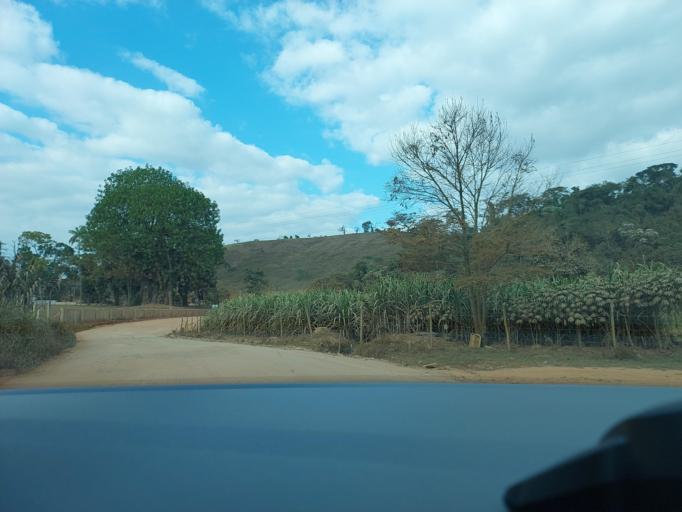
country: BR
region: Minas Gerais
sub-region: Visconde Do Rio Branco
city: Visconde do Rio Branco
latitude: -20.8525
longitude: -42.6678
